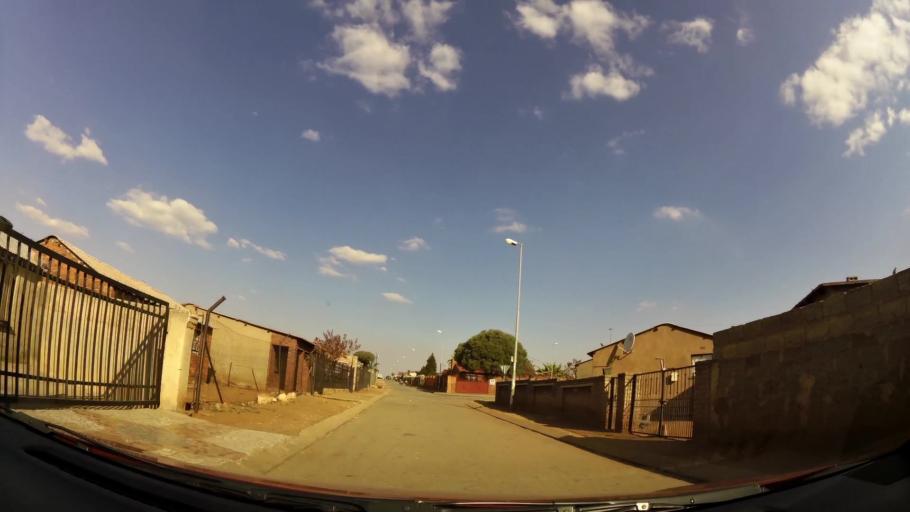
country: ZA
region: Gauteng
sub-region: City of Johannesburg Metropolitan Municipality
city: Soweto
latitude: -26.2272
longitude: 27.8731
